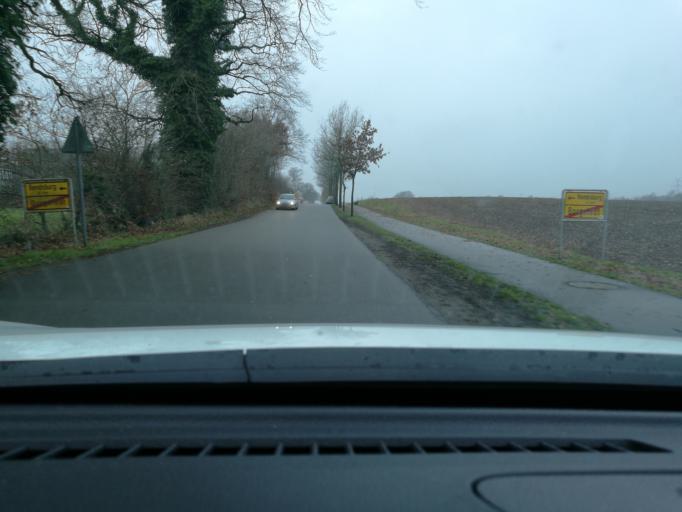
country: DE
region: Schleswig-Holstein
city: Borgstedt
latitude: 54.3345
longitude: 9.7045
